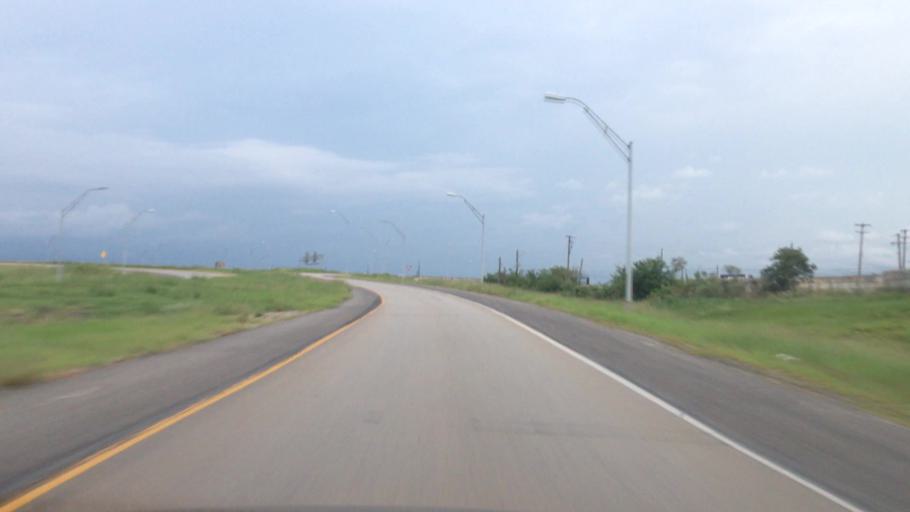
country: US
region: Texas
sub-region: Tarrant County
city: Saginaw
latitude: 32.8349
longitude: -97.3613
